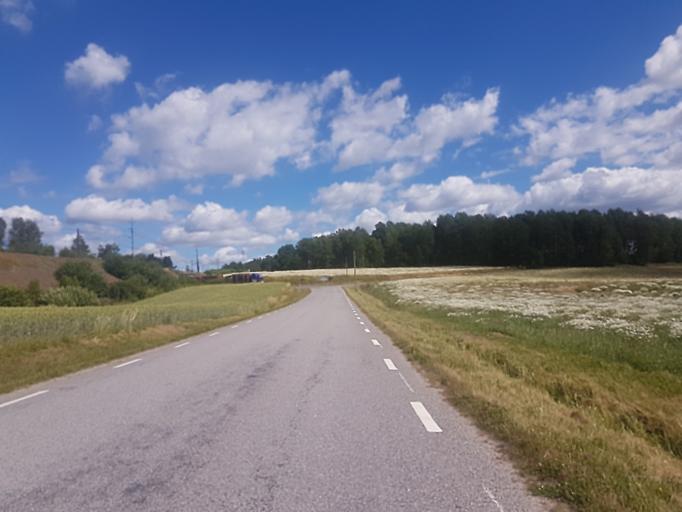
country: SE
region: Soedermanland
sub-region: Gnesta Kommun
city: Gnesta
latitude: 59.0453
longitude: 17.3358
